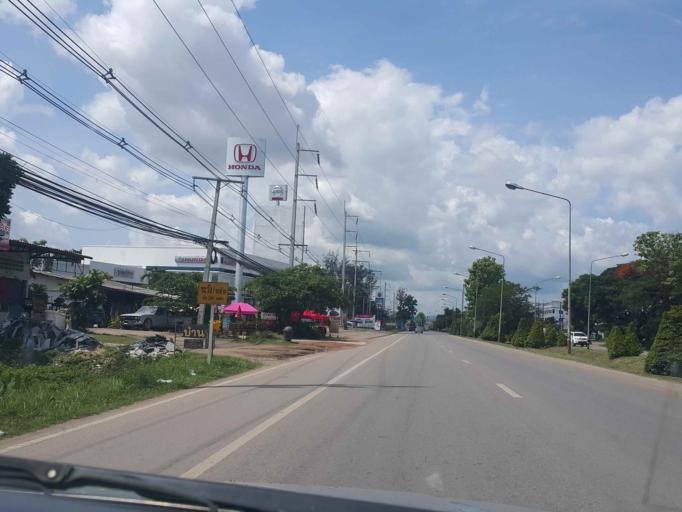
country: TH
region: Phayao
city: Phayao
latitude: 19.1495
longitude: 99.9125
